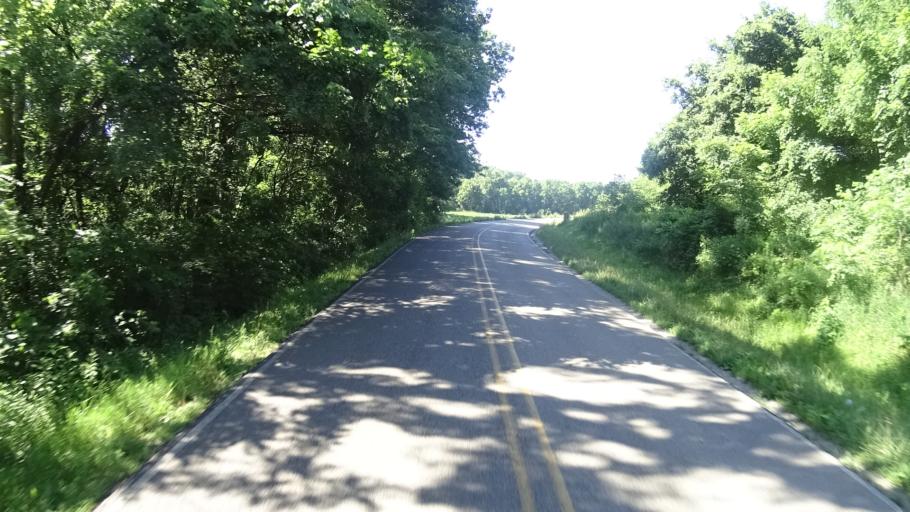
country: US
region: Indiana
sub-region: Madison County
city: Pendleton
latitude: 39.9972
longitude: -85.7563
